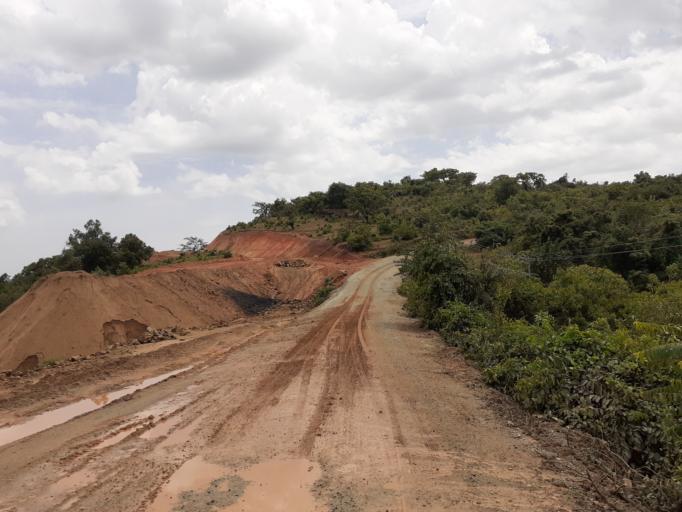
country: ET
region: Oromiya
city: Gimbi
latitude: 9.3203
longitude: 35.6927
